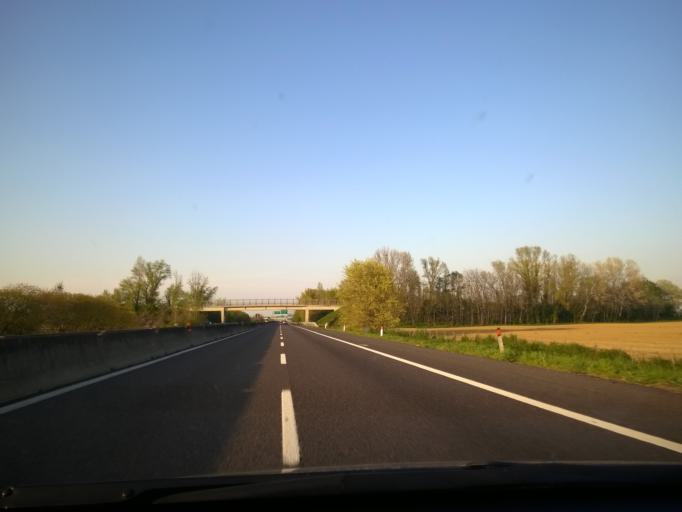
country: IT
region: Emilia-Romagna
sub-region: Provincia di Bologna
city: Progresso
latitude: 44.5818
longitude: 11.3939
